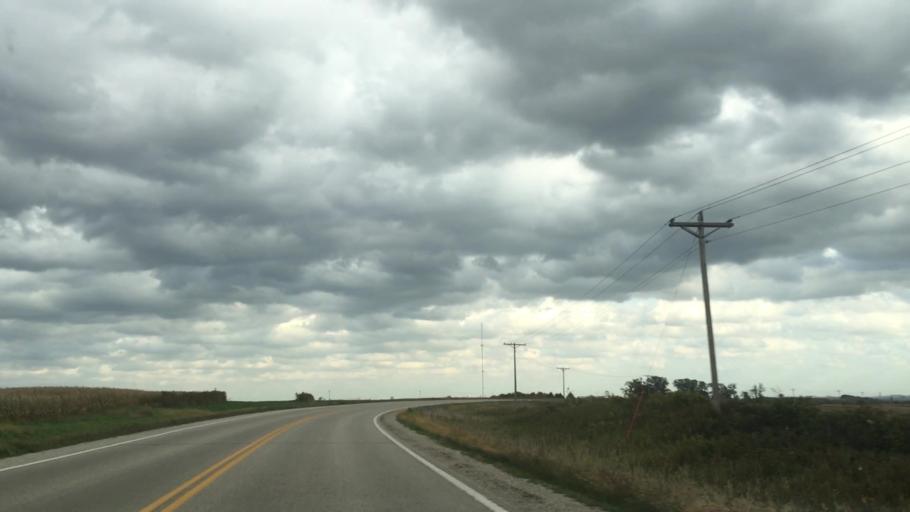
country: US
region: Minnesota
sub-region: Fillmore County
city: Preston
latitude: 43.7353
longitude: -92.1013
